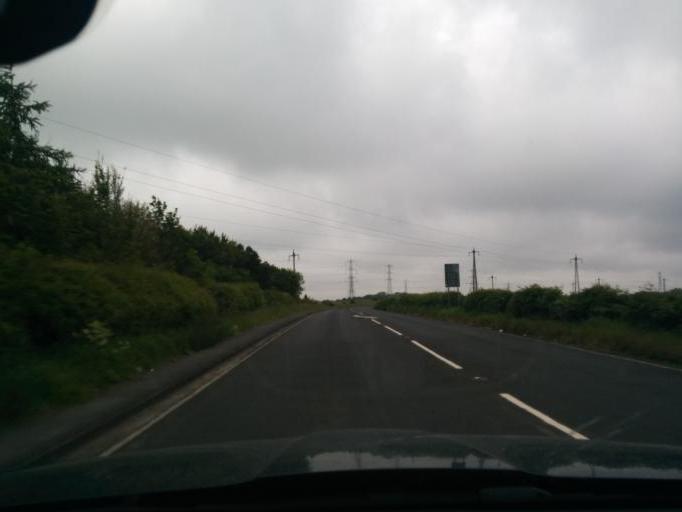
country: GB
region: England
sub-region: Northumberland
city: Bedlington
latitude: 55.1211
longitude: -1.5766
